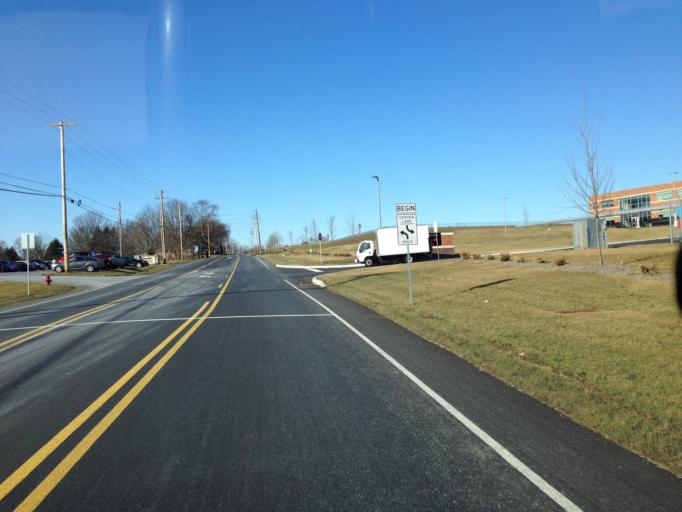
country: US
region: Pennsylvania
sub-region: Lancaster County
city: Manheim
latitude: 40.1733
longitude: -76.3710
